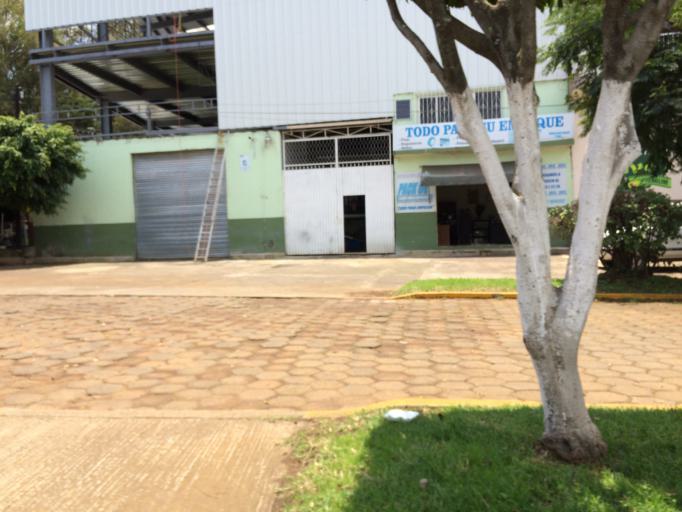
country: MX
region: Michoacan
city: Periban de Ramos
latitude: 19.5264
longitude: -102.4131
